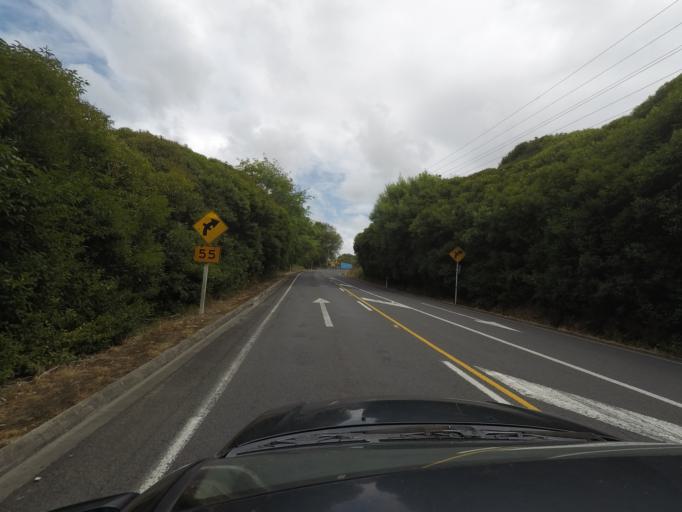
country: NZ
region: Auckland
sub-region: Auckland
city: Parakai
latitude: -36.6250
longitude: 174.5021
